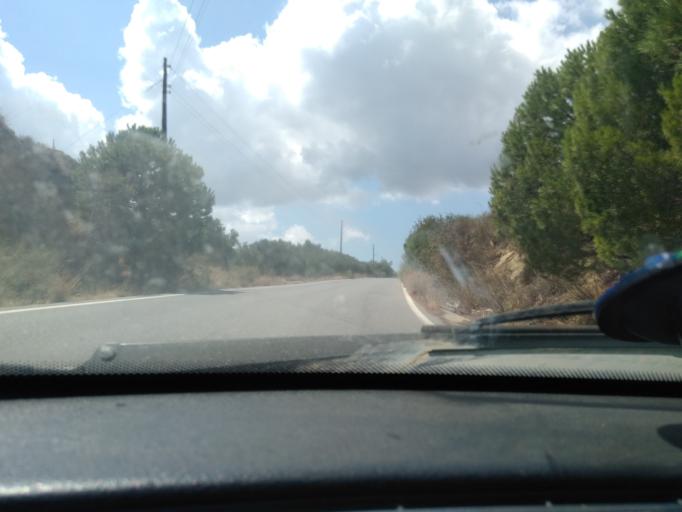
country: GR
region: Crete
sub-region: Nomos Lasithiou
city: Siteia
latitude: 35.1256
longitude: 26.0661
